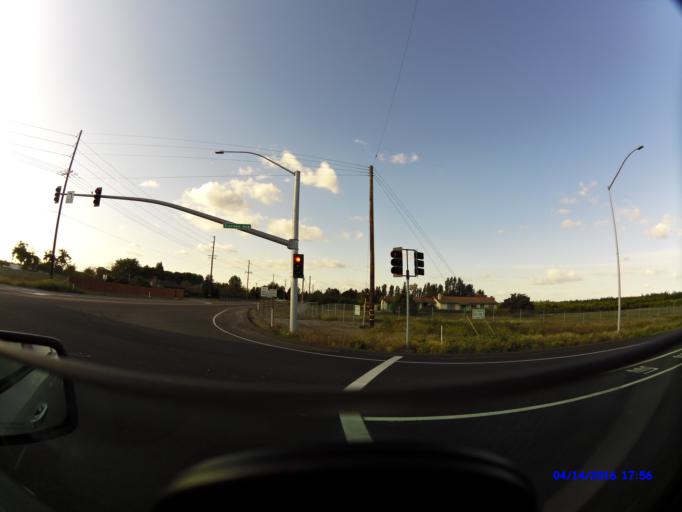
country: US
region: California
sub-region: Stanislaus County
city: Del Rio
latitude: 37.7114
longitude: -121.0128
